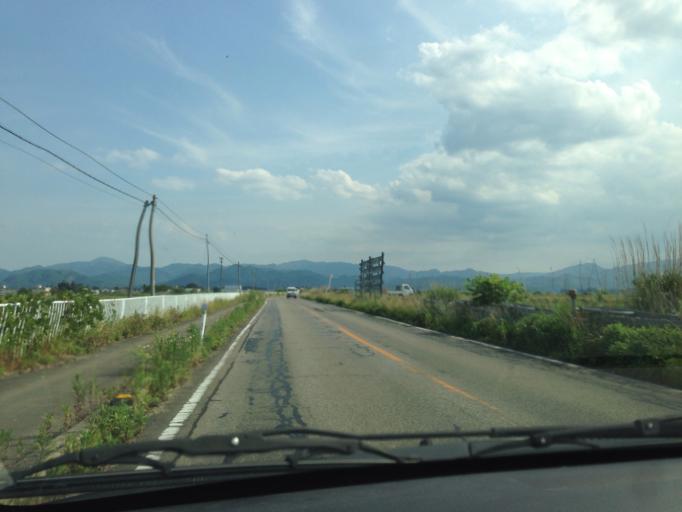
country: JP
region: Fukushima
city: Kitakata
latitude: 37.4766
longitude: 139.8395
